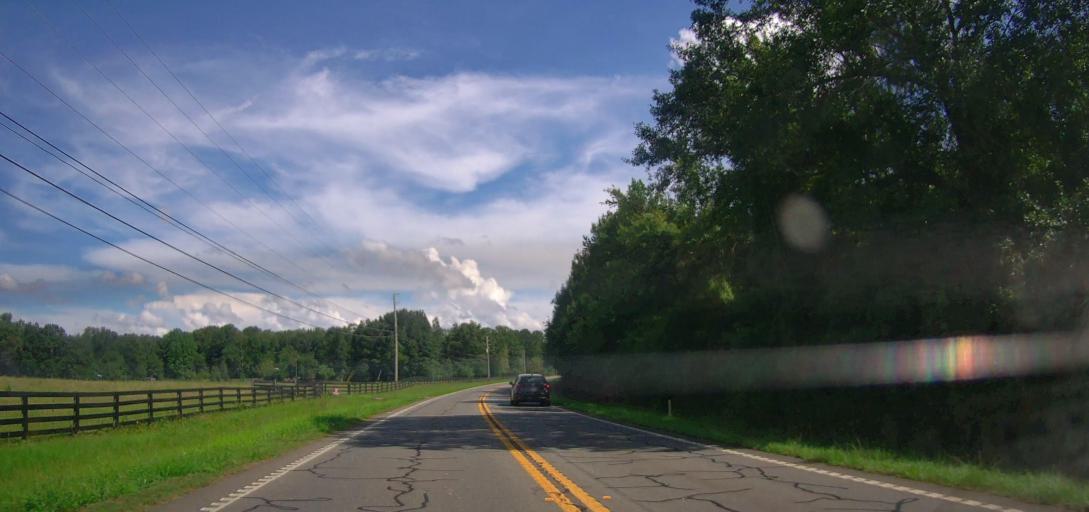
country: US
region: Georgia
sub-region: Talbot County
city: Sardis
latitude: 32.7970
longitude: -84.5707
